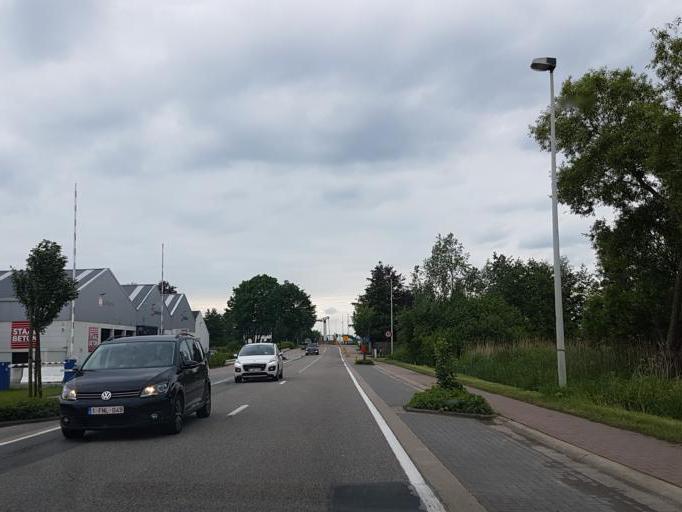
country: BE
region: Flanders
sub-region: Provincie Antwerpen
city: Rijkevorsel
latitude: 51.3325
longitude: 4.7481
